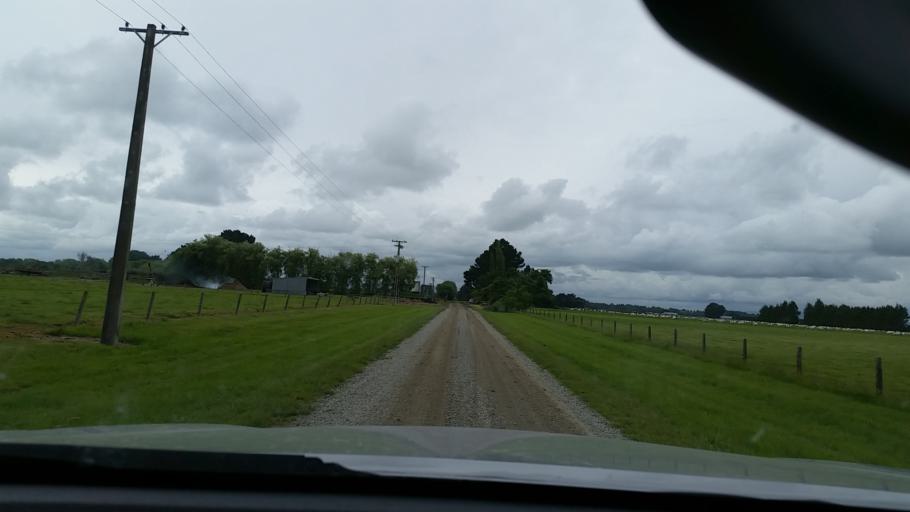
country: NZ
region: Southland
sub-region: Southland District
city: Winton
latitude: -46.1800
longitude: 168.2818
